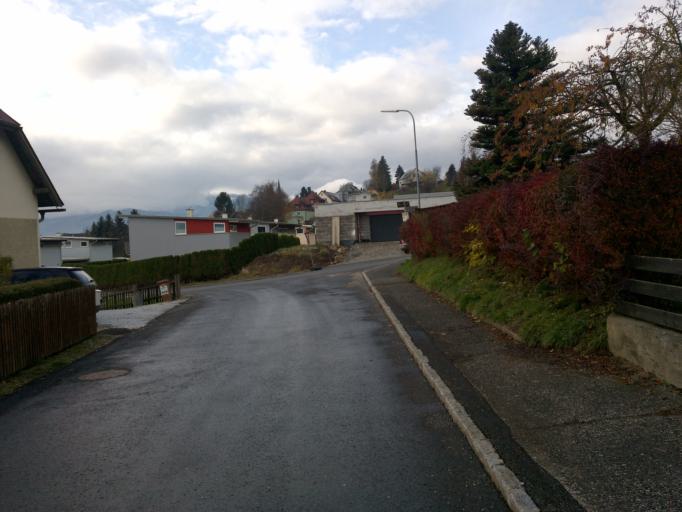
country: AT
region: Styria
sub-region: Politischer Bezirk Murtal
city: Fohnsdorf
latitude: 47.2119
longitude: 14.6837
